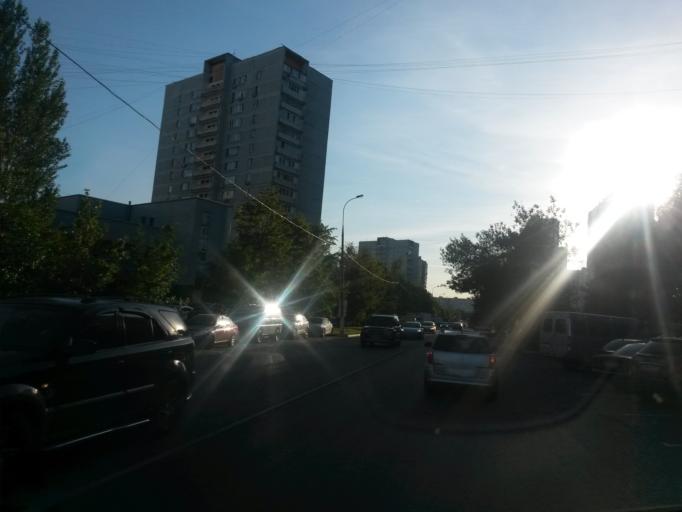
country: RU
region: Moscow
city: Orekhovo-Borisovo
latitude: 55.6102
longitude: 37.7313
